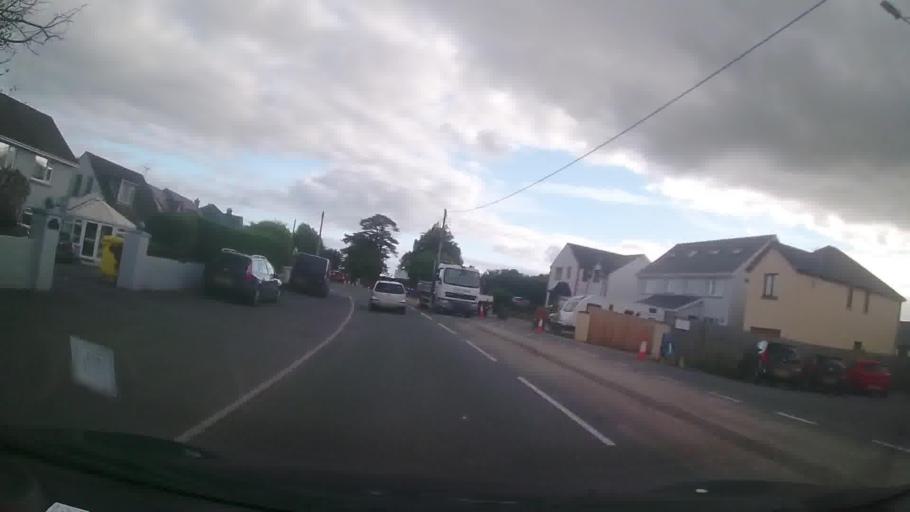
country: GB
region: Wales
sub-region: Pembrokeshire
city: Kilgetty
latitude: 51.7156
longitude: -4.7332
